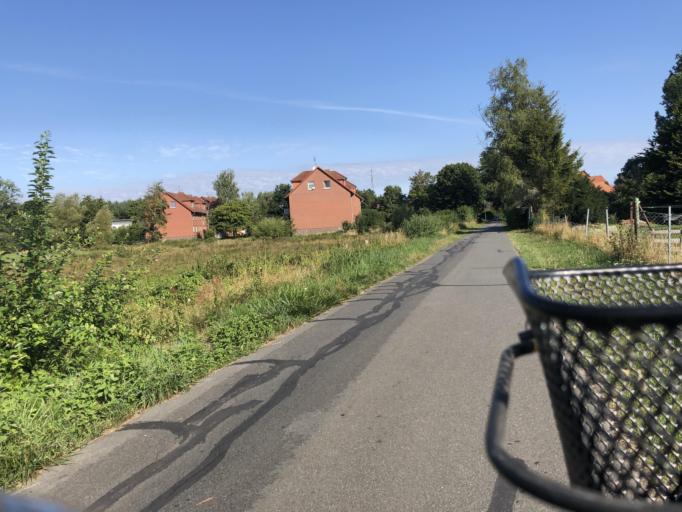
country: DE
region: Lower Saxony
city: Dahlenburg
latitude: 53.1834
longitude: 10.7435
